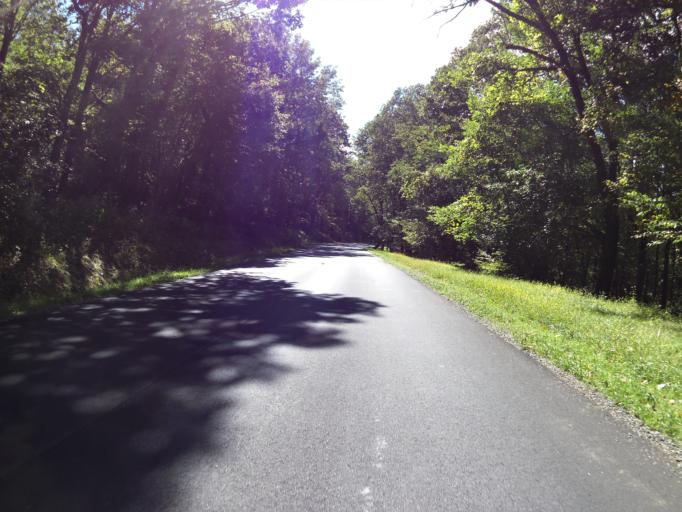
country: US
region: Virginia
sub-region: Page County
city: Luray
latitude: 38.6785
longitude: -78.3303
